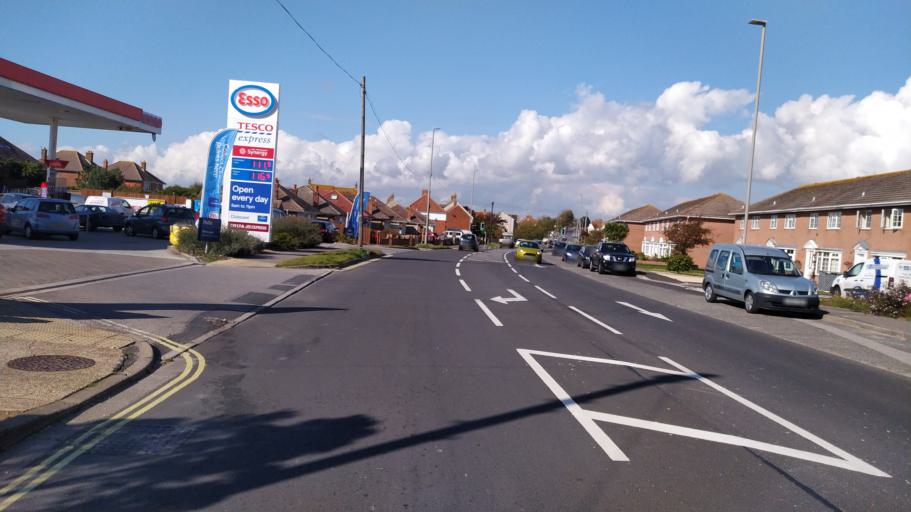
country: GB
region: England
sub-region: Dorset
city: Weymouth
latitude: 50.6048
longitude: -2.4841
